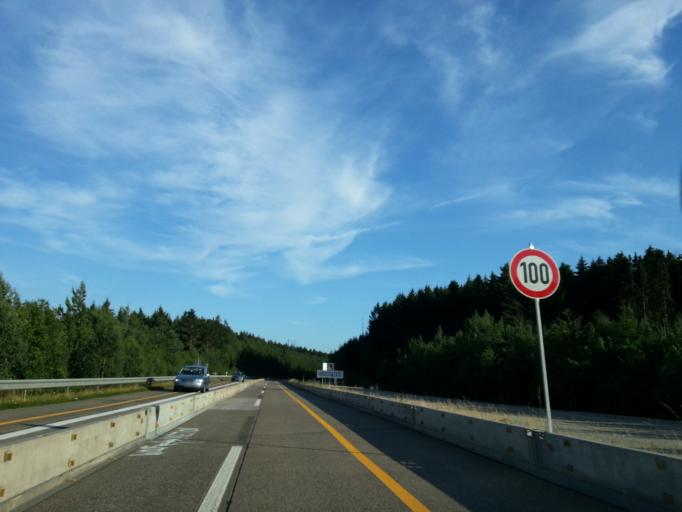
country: DE
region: Rheinland-Pfalz
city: Hinzert-Polert
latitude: 49.7209
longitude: 6.8909
